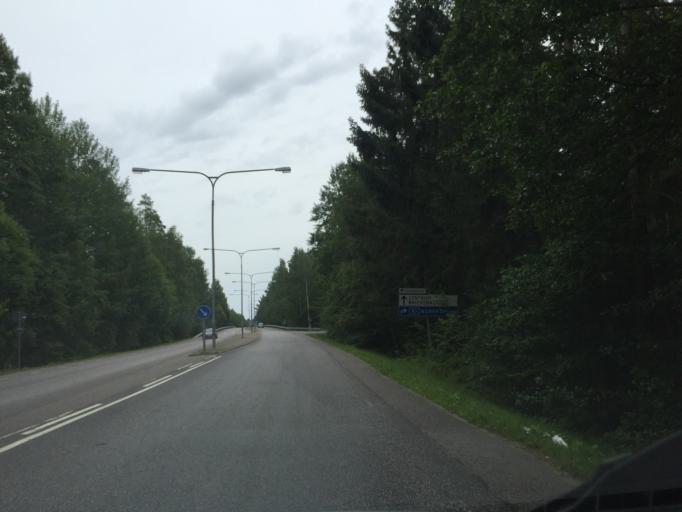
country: SE
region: OErebro
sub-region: Orebro Kommun
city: Orebro
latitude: 59.2452
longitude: 15.2301
